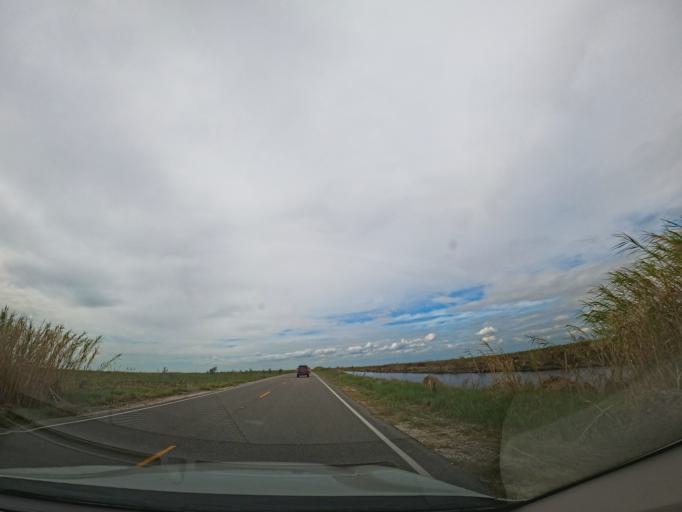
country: US
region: Louisiana
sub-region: Cameron Parish
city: Cameron
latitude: 29.7702
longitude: -93.4276
